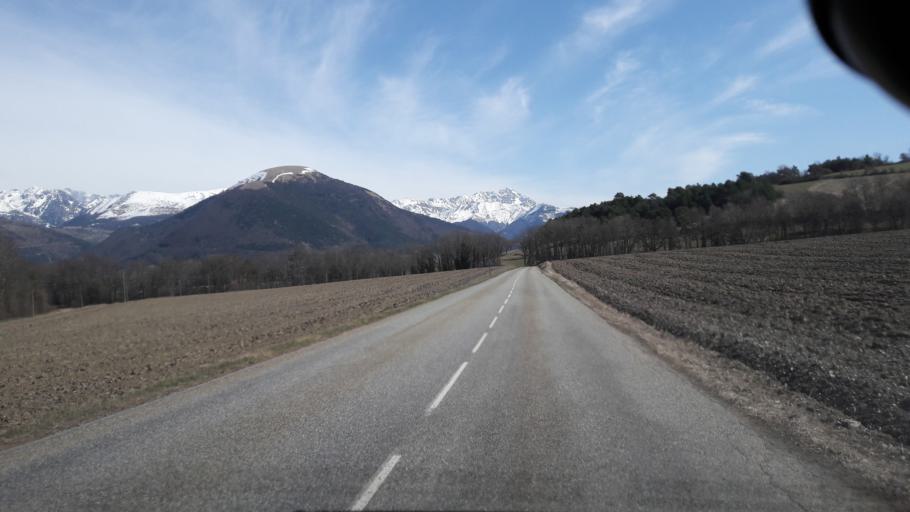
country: FR
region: Rhone-Alpes
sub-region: Departement de l'Isere
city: La Mure
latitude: 44.8442
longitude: 5.8123
